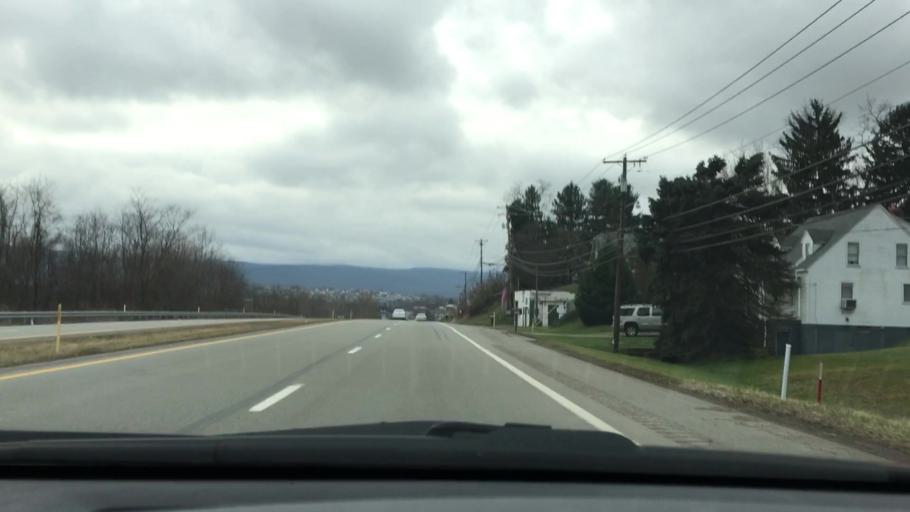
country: US
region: Pennsylvania
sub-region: Fayette County
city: Oliver
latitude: 39.9331
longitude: -79.7295
